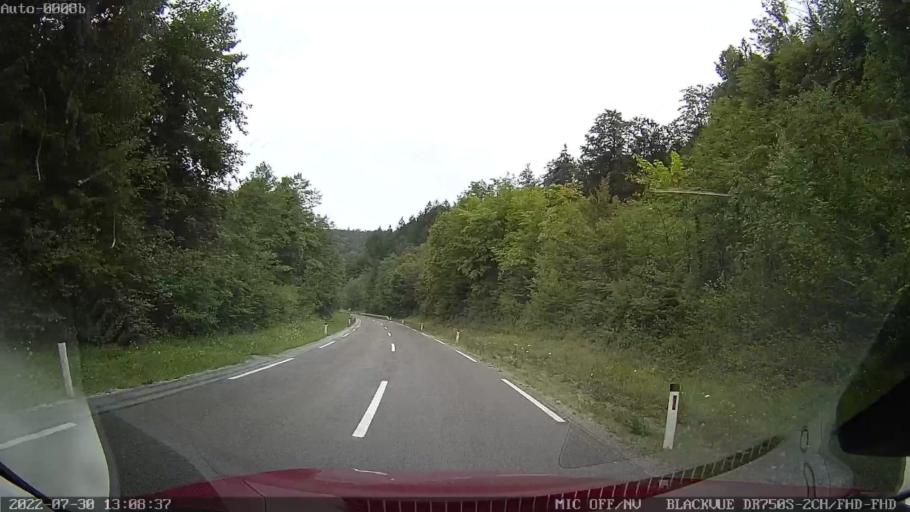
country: SI
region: Dolenjske Toplice
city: Dolenjske Toplice
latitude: 45.6789
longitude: 15.0982
